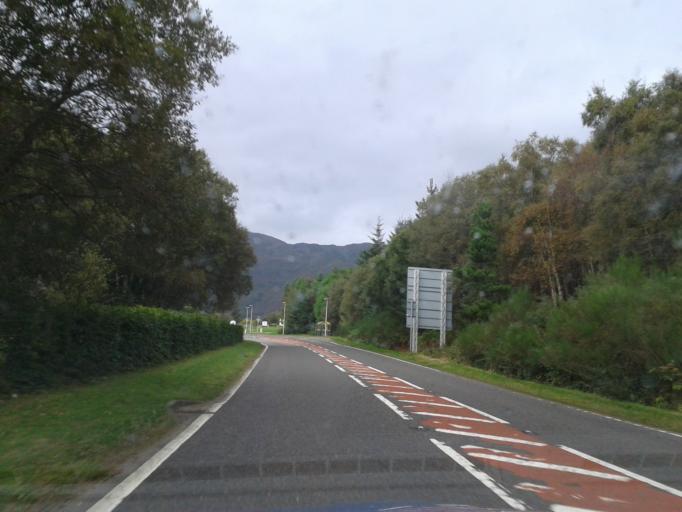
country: GB
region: Scotland
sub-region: Highland
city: Fort William
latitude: 57.2749
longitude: -5.5132
